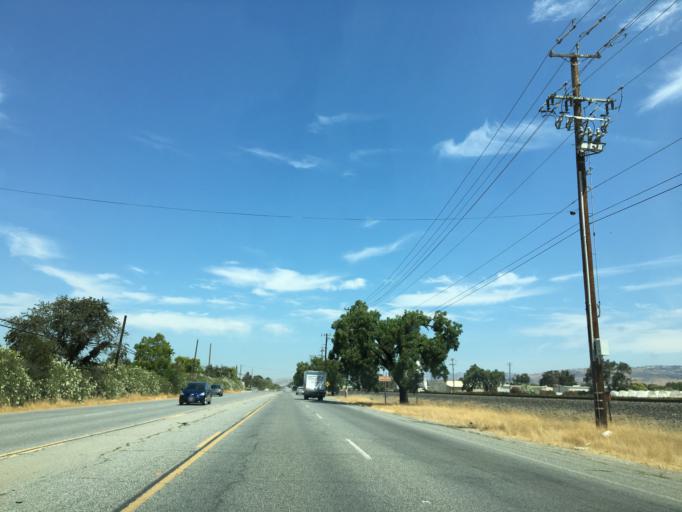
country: US
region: California
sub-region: Santa Clara County
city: Gilroy
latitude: 37.0394
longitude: -121.5850
